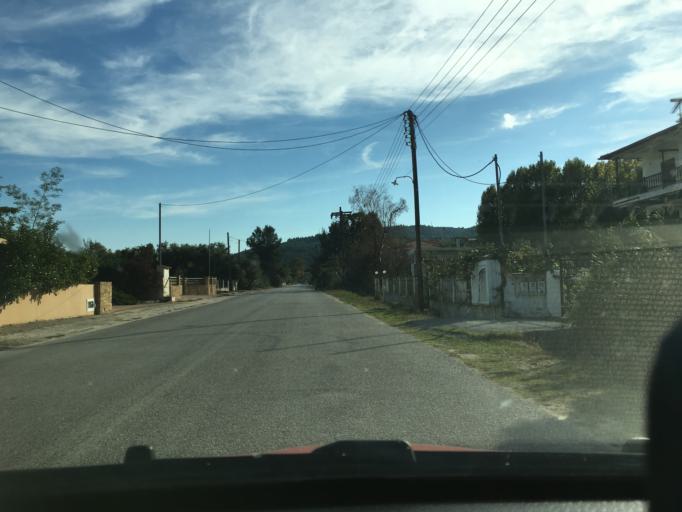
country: GR
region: Central Macedonia
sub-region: Nomos Chalkidikis
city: Agios Nikolaos
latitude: 40.2967
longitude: 23.6942
